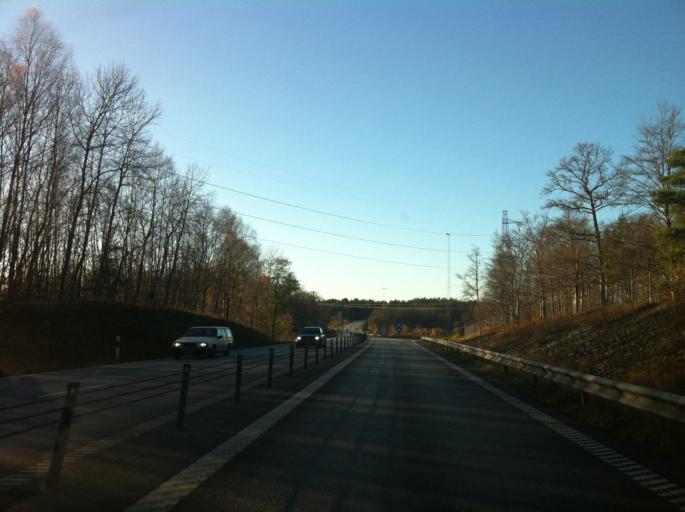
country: SE
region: Blekinge
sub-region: Karlshamns Kommun
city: Karlshamn
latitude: 56.1871
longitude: 14.8268
